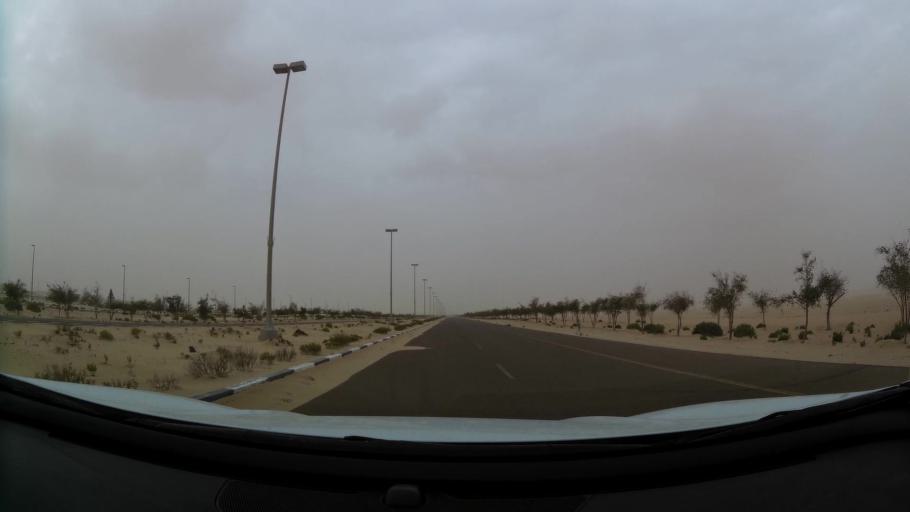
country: AE
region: Abu Dhabi
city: Abu Dhabi
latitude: 24.4252
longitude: 54.7074
